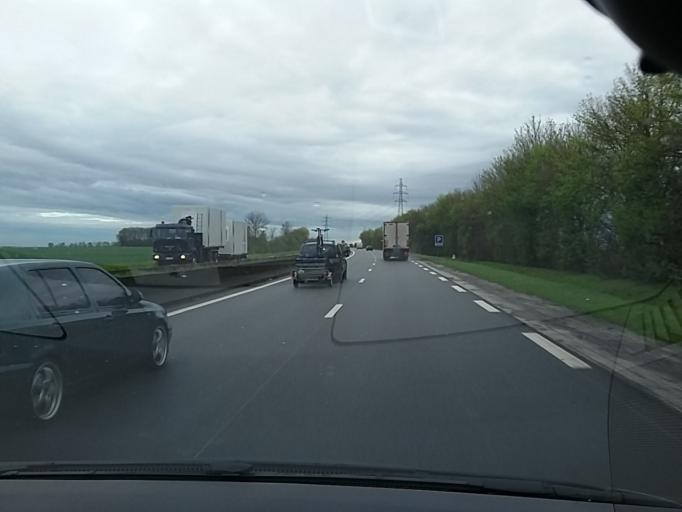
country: FR
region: Picardie
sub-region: Departement de la Somme
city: Rivery
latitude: 49.9231
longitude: 2.3299
